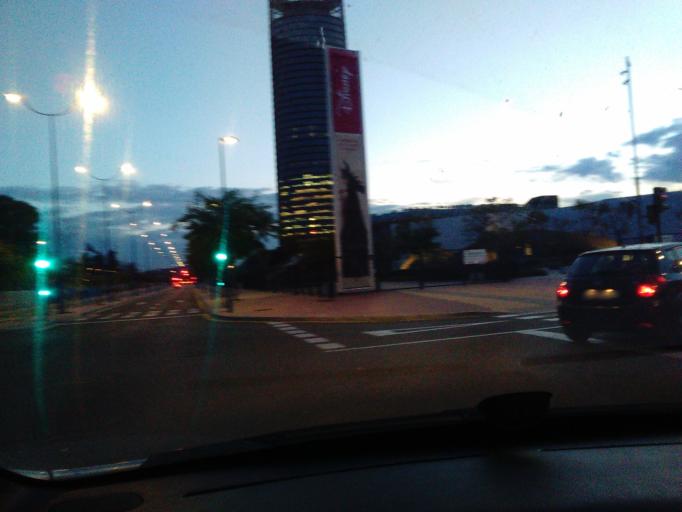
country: ES
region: Andalusia
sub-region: Provincia de Sevilla
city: Camas
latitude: 37.3942
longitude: -6.0086
